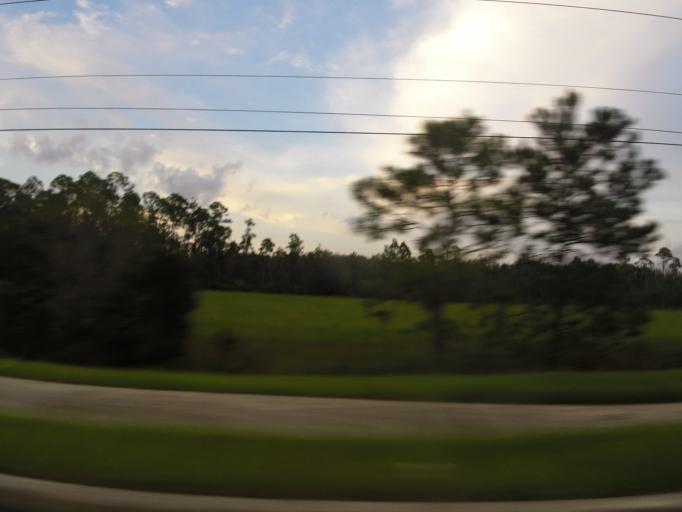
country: US
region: Florida
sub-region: Saint Johns County
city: Fruit Cove
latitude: 30.0899
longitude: -81.5352
